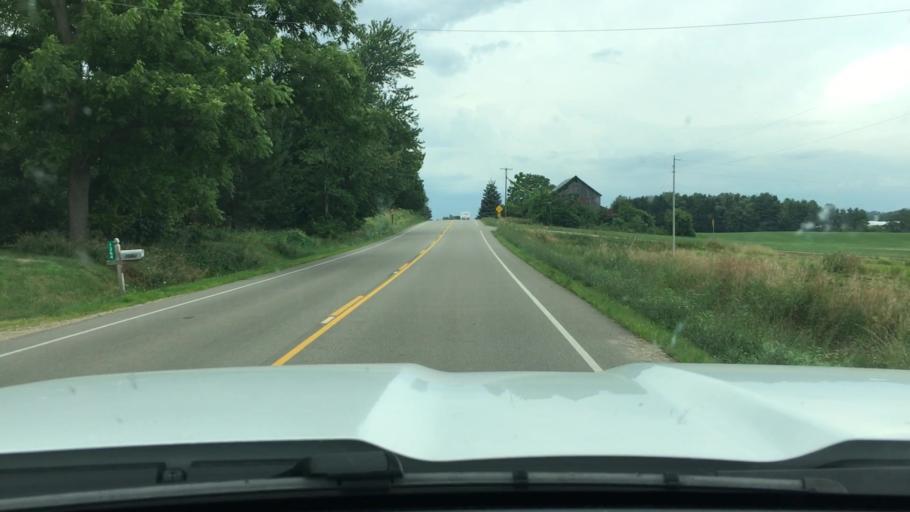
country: US
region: Michigan
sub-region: Kent County
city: Byron Center
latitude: 42.7824
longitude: -85.8160
